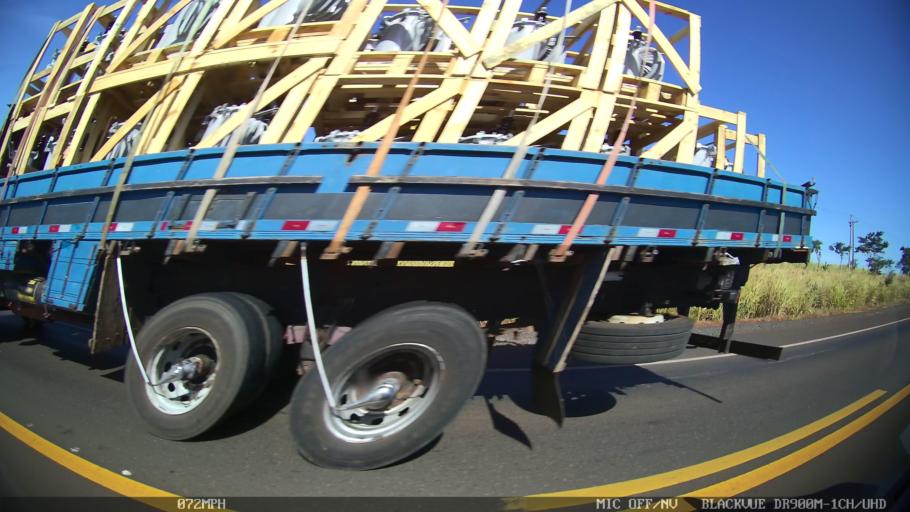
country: BR
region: Sao Paulo
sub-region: Olimpia
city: Olimpia
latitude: -20.6372
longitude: -48.8216
